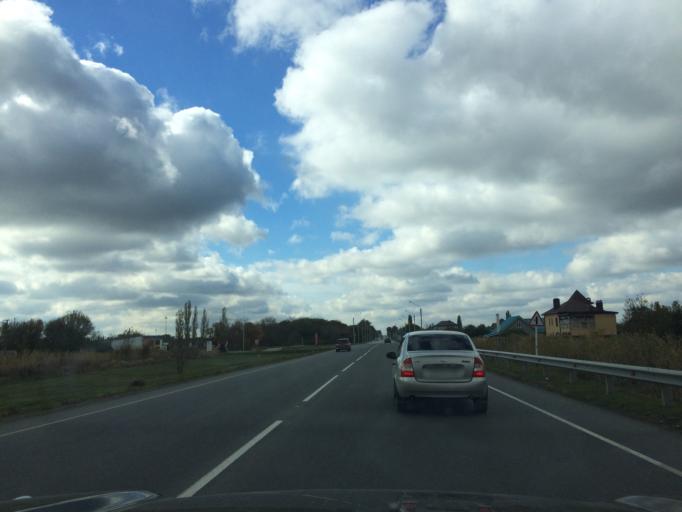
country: RU
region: Rostov
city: Bataysk
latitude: 47.1123
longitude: 39.6574
